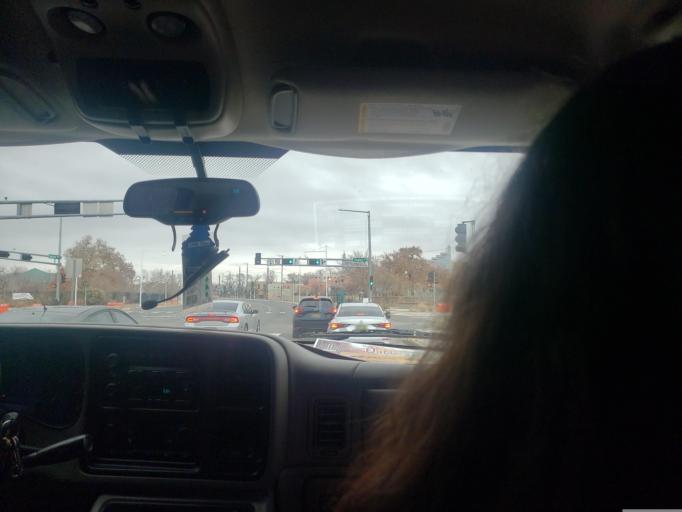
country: US
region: New Mexico
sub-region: Bernalillo County
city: Albuquerque
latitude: 35.0909
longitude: -106.6793
